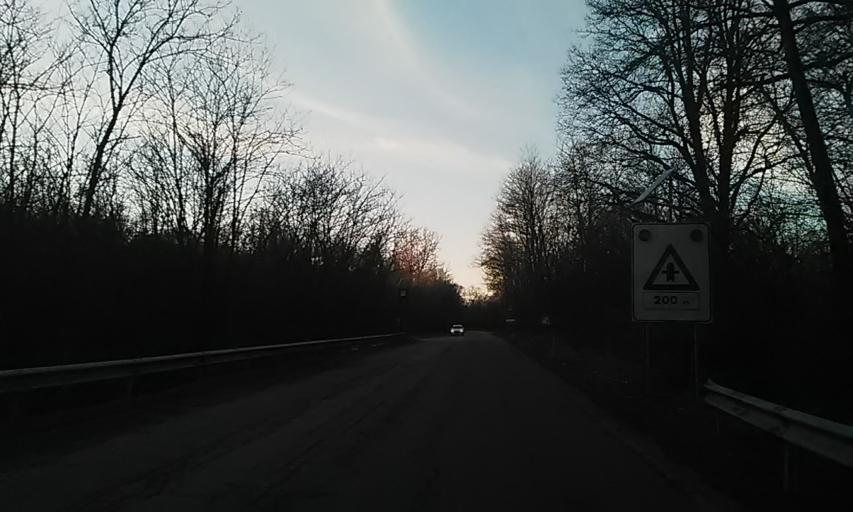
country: IT
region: Piedmont
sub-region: Provincia di Biella
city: Masserano
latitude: 45.5643
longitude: 8.2297
